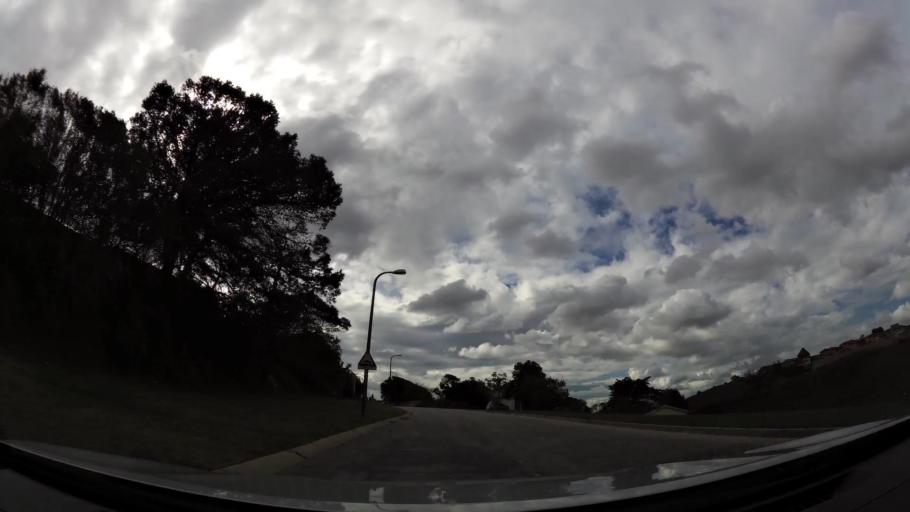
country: ZA
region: Eastern Cape
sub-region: Nelson Mandela Bay Metropolitan Municipality
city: Port Elizabeth
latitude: -33.9344
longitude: 25.5203
